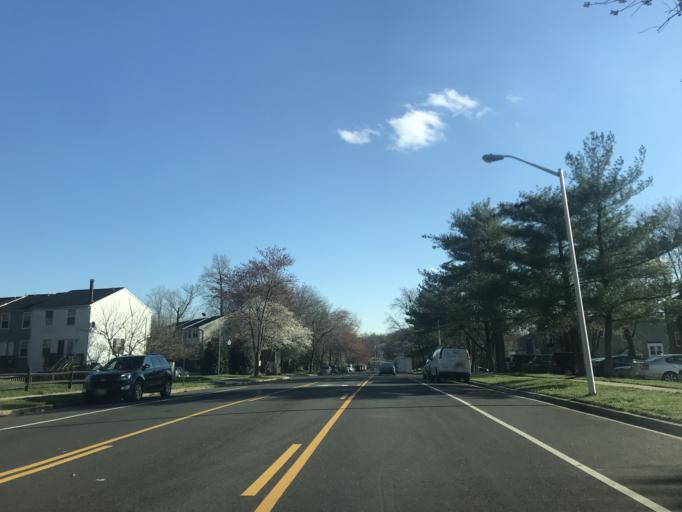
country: US
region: Maryland
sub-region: Prince George's County
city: Kettering
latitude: 38.8943
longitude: -76.8074
